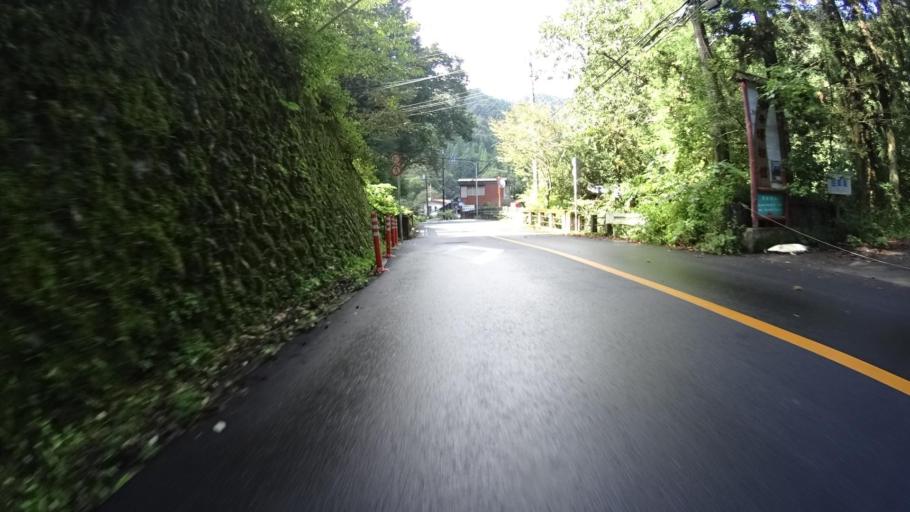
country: JP
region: Tokyo
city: Itsukaichi
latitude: 35.7325
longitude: 139.1111
